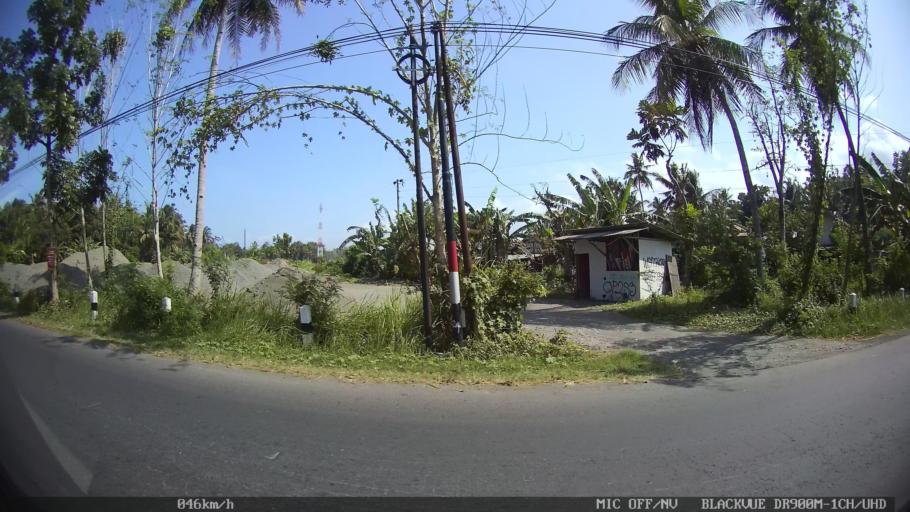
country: ID
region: Daerah Istimewa Yogyakarta
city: Srandakan
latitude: -7.9463
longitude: 110.2250
